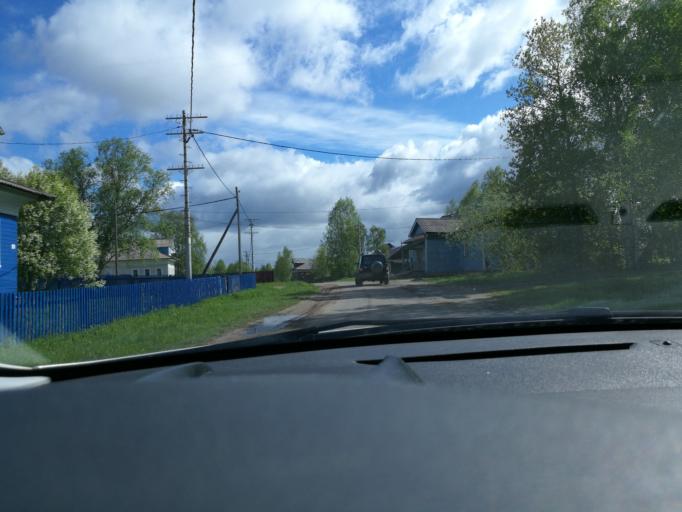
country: RU
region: Arkhangelskaya
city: Kholmogory
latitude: 64.2305
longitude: 41.7400
